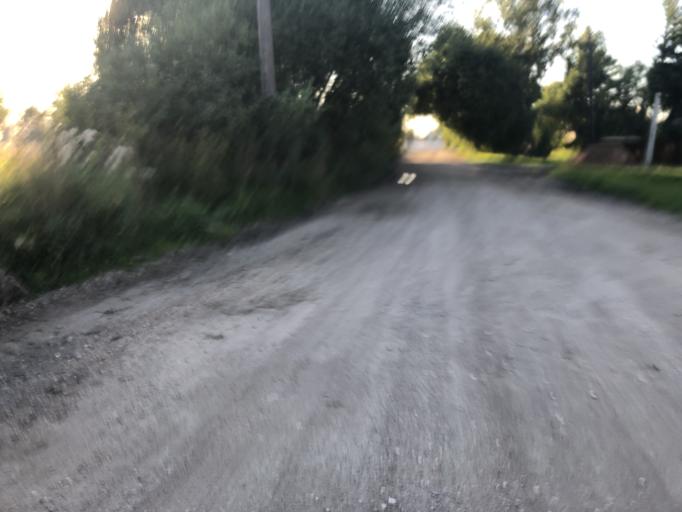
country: RU
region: Tverskaya
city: Rzhev
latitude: 56.2451
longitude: 34.3036
